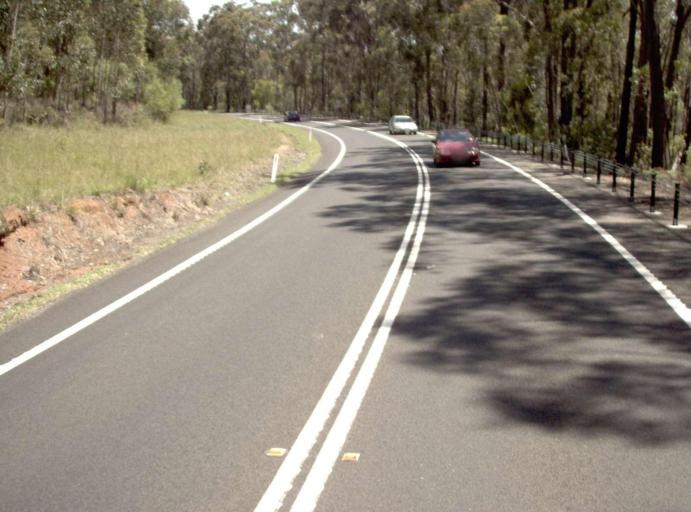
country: AU
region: Victoria
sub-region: East Gippsland
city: Lakes Entrance
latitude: -37.6953
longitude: 148.5906
